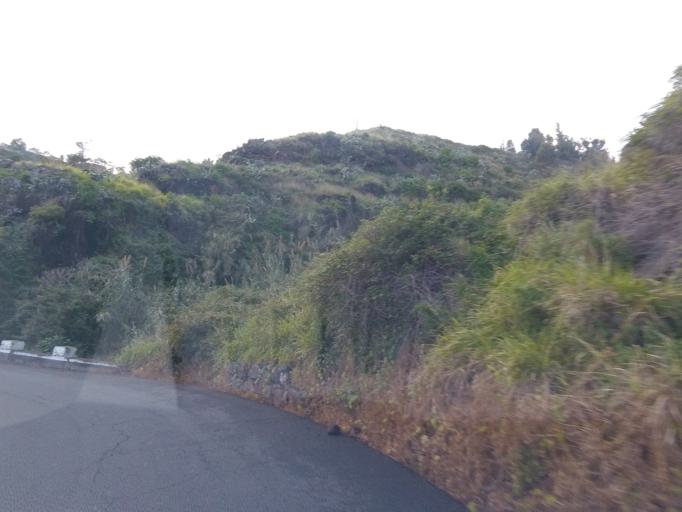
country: PT
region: Madeira
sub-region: Machico
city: Machico
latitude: 32.7047
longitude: -16.7716
